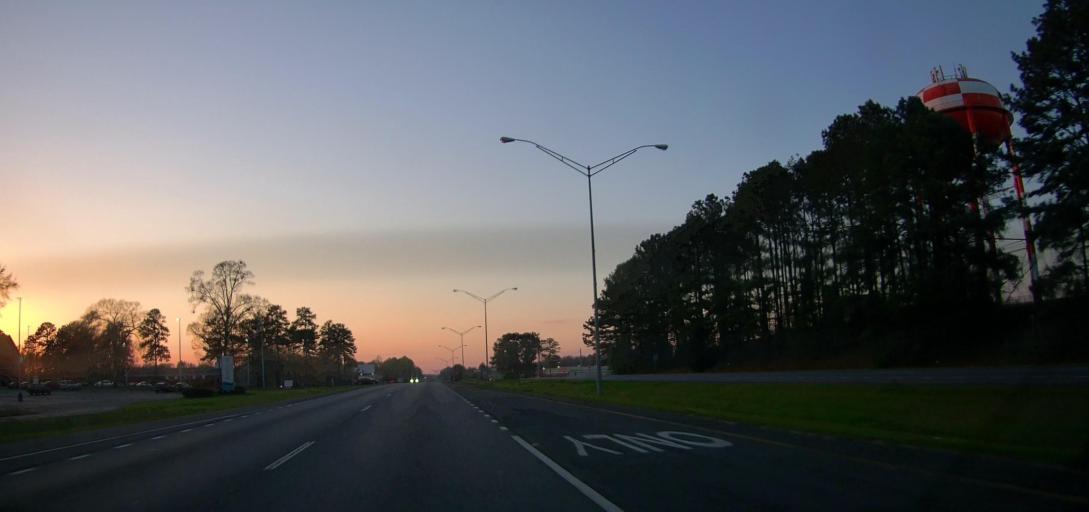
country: US
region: Alabama
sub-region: Tallapoosa County
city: Alexander City
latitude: 32.9308
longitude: -85.9681
